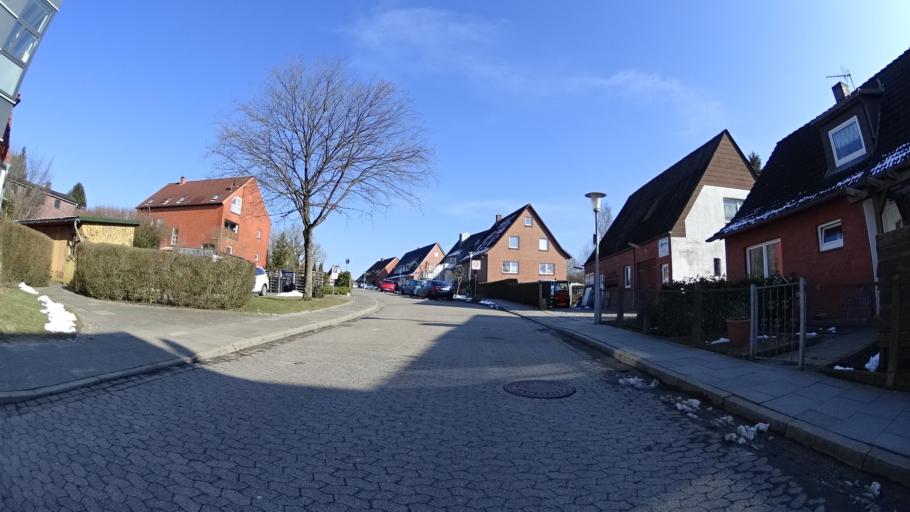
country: DE
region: Schleswig-Holstein
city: Preetz
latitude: 54.2360
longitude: 10.2862
